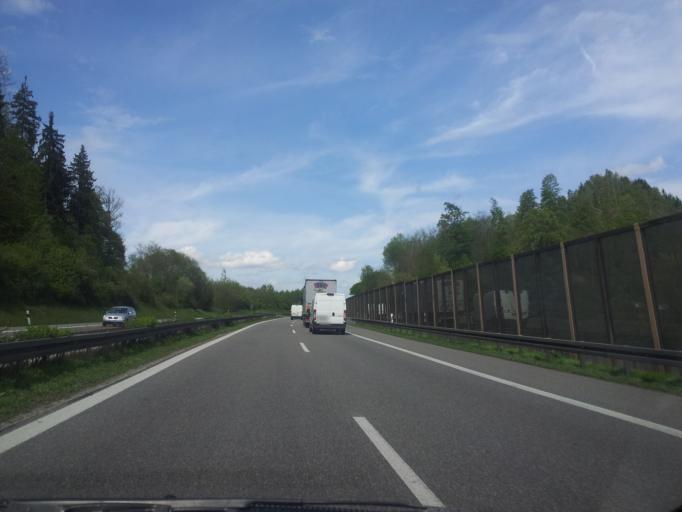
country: DE
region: Baden-Wuerttemberg
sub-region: Tuebingen Region
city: Aichstetten
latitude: 47.8921
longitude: 10.0457
